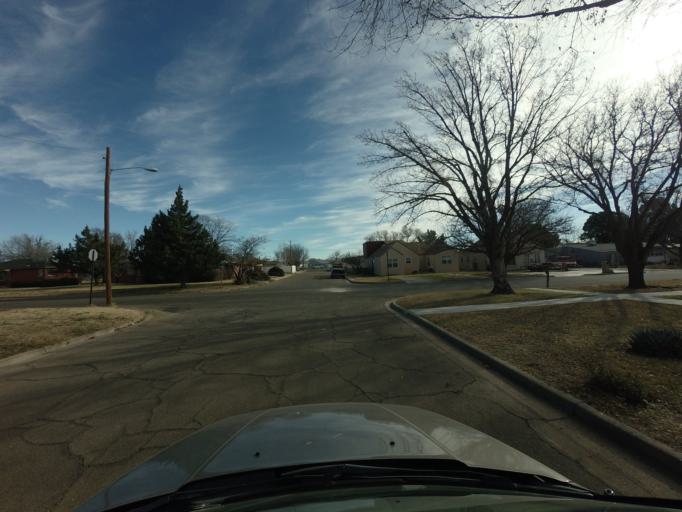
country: US
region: New Mexico
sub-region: Curry County
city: Clovis
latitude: 34.4173
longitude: -103.2018
